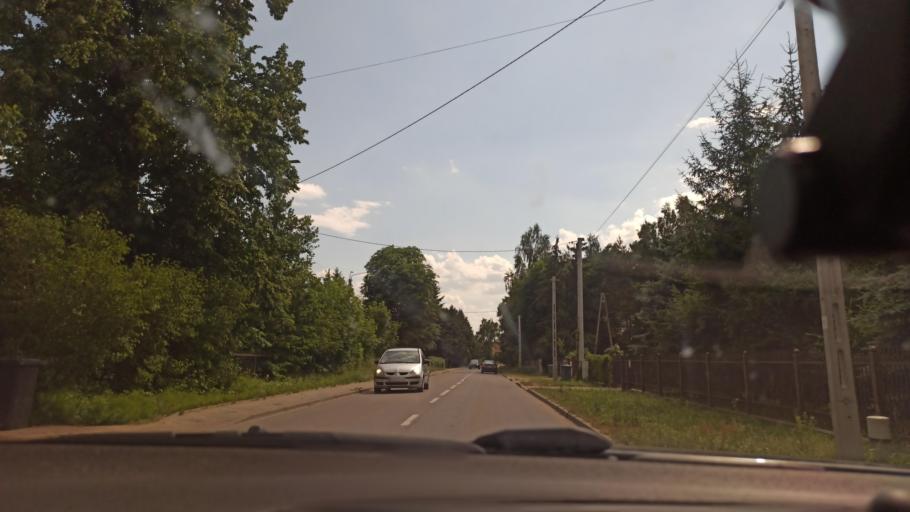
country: PL
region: Podlasie
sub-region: Powiat bialostocki
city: Turosn Koscielna
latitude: 53.0679
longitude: 23.1002
